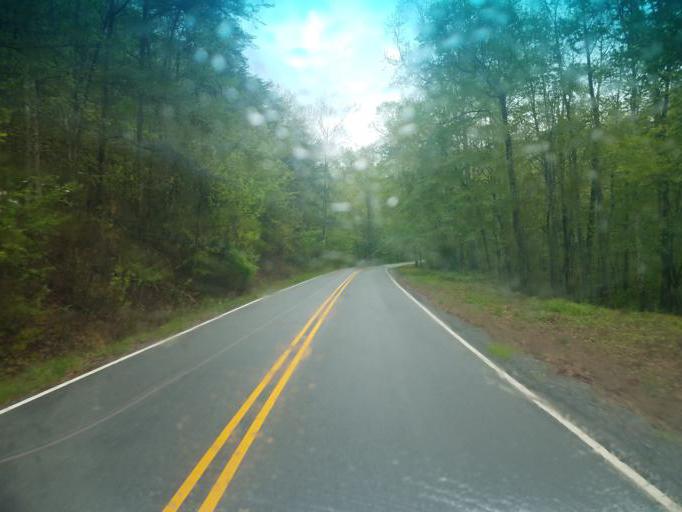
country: US
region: Tennessee
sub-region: Johnson County
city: Mountain City
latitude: 36.6263
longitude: -81.7669
